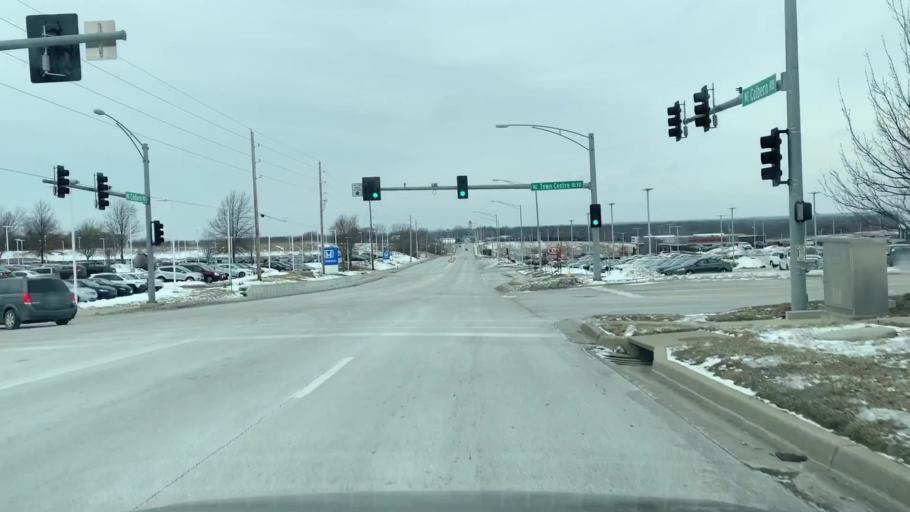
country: US
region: Missouri
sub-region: Jackson County
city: Lees Summit
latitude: 38.9465
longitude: -94.3693
